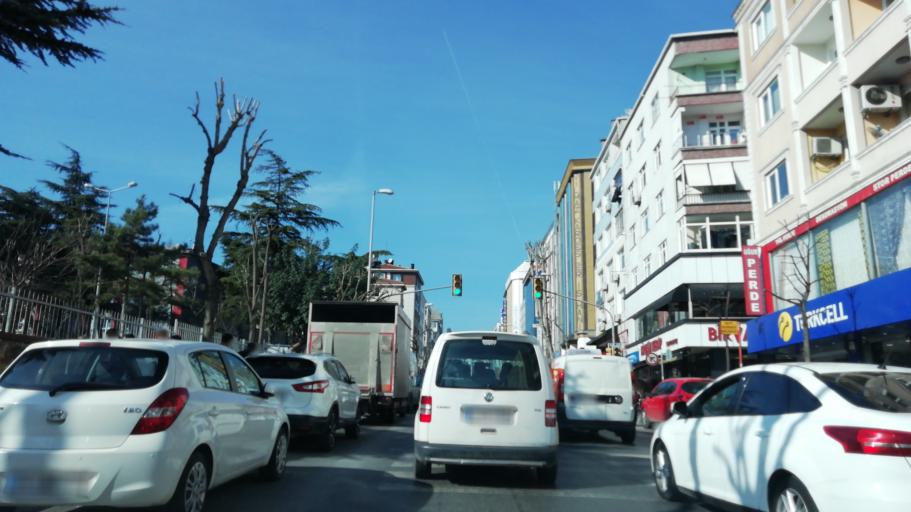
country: TR
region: Istanbul
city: Bahcelievler
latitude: 40.9964
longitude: 28.8348
